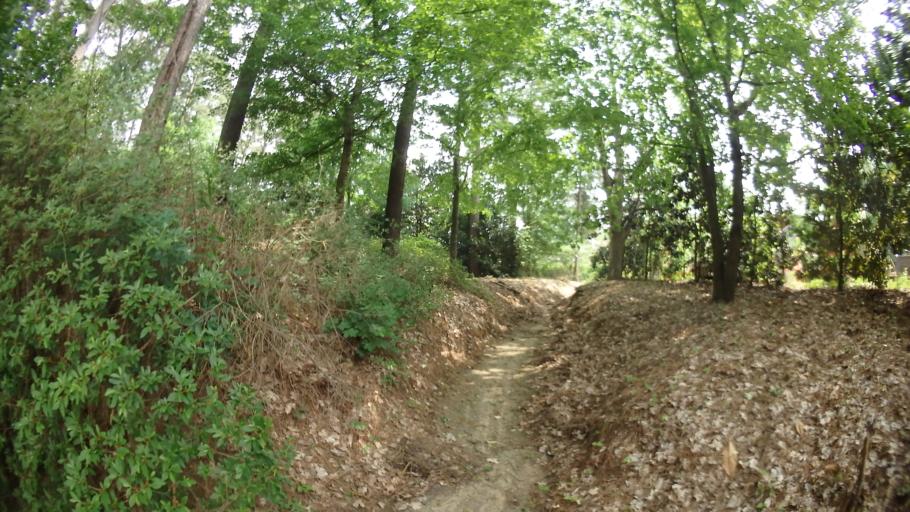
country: US
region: Texas
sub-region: Nacogdoches County
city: Nacogdoches
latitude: 31.6195
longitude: -94.6405
